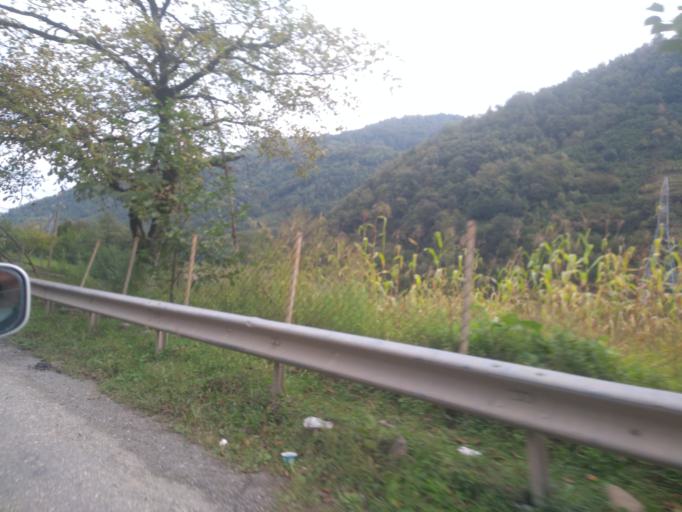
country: TR
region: Artvin
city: Muratli
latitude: 41.5467
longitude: 41.7910
